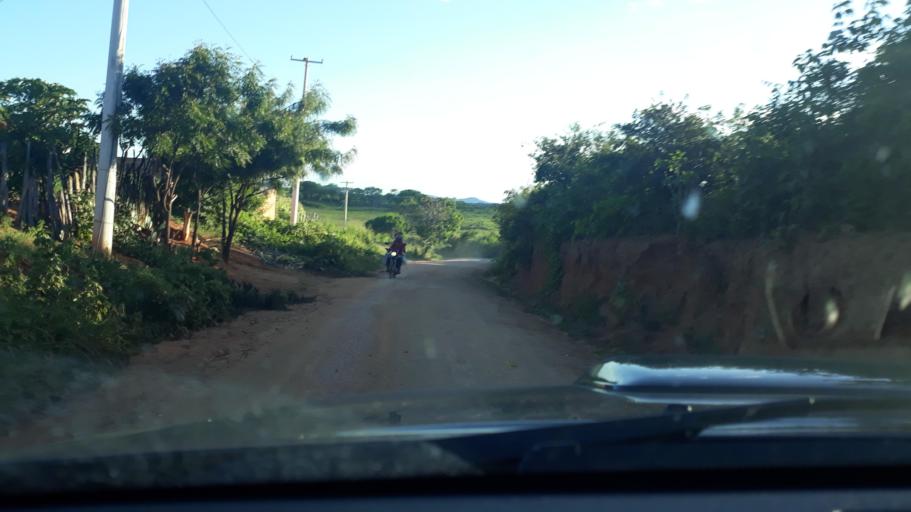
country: BR
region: Bahia
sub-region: Riacho De Santana
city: Riacho de Santana
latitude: -13.7953
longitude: -42.7119
